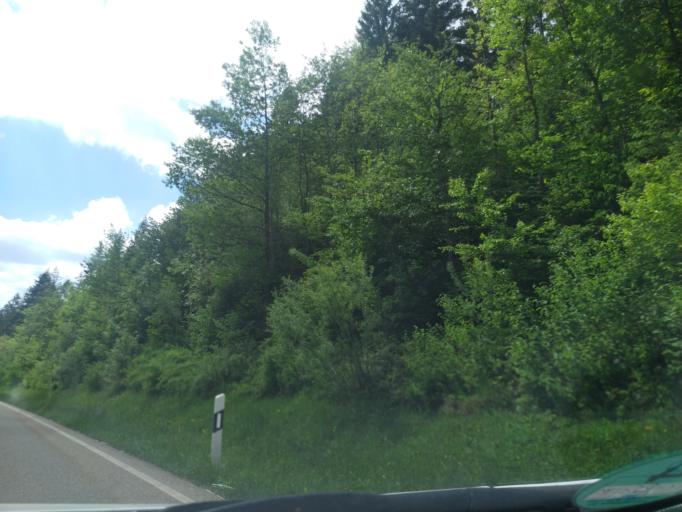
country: DE
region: Baden-Wuerttemberg
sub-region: Karlsruhe Region
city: Freudenstadt
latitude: 48.4912
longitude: 8.4150
